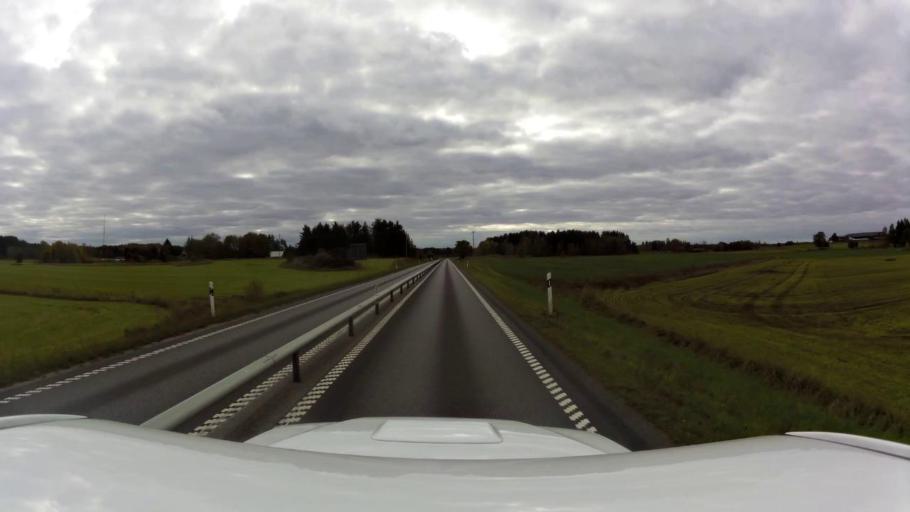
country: SE
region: OEstergoetland
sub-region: Linkopings Kommun
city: Malmslatt
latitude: 58.3288
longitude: 15.5632
